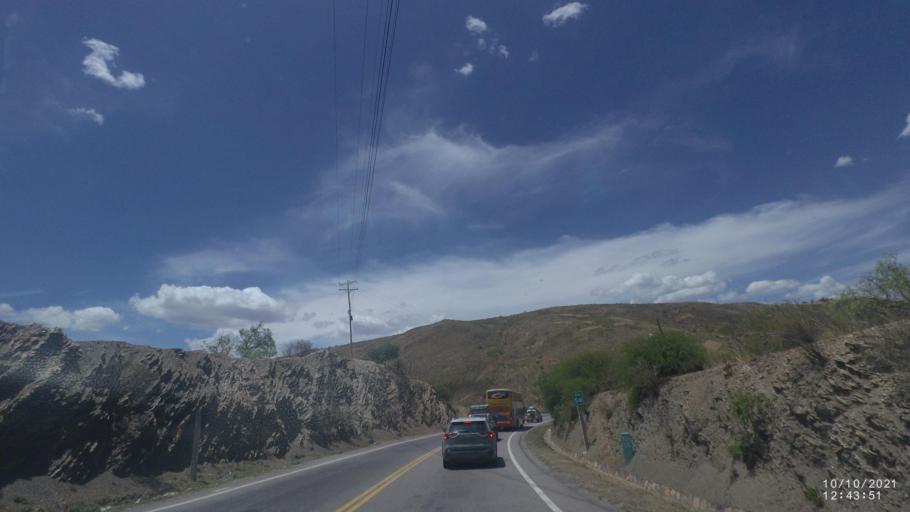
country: BO
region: Cochabamba
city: Irpa Irpa
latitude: -17.6300
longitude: -66.3820
